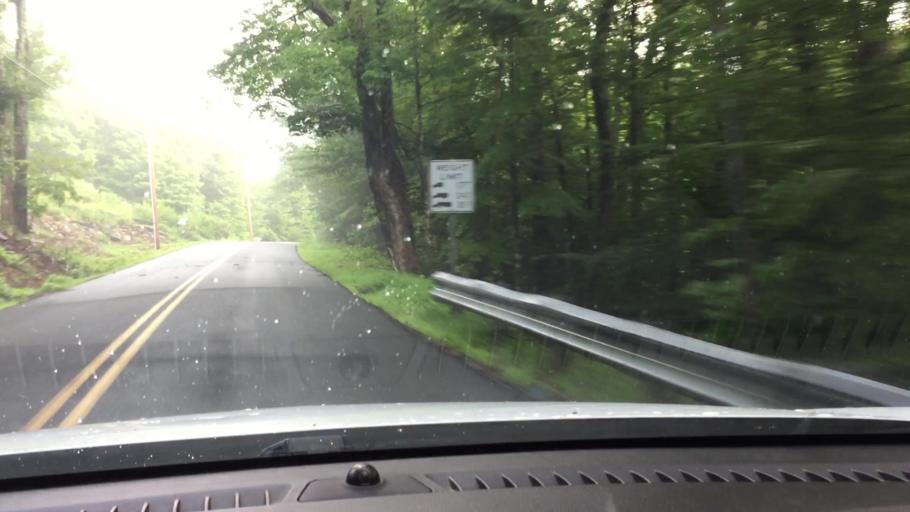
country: US
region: Massachusetts
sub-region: Berkshire County
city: Becket
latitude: 42.4177
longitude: -72.9835
